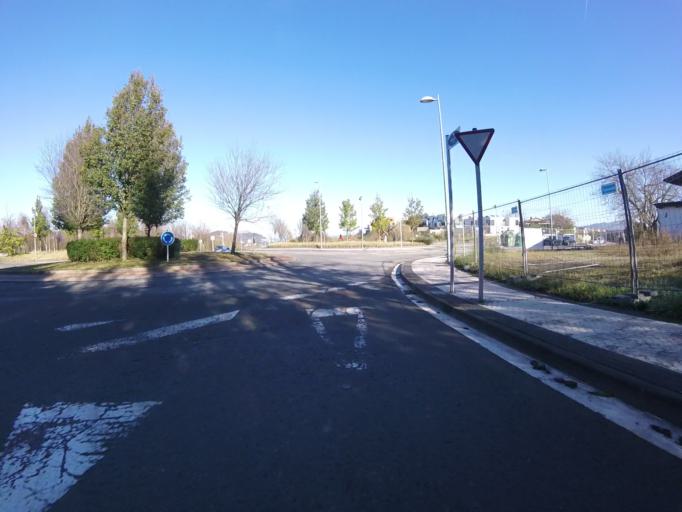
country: ES
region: Basque Country
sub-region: Provincia de Guipuzcoa
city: Lasarte
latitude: 43.2915
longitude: -2.0047
